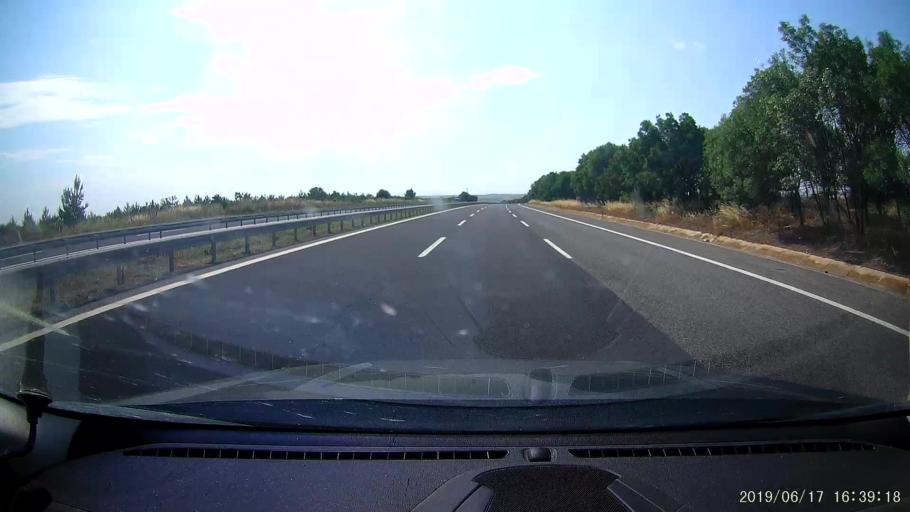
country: TR
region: Kirklareli
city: Luleburgaz
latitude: 41.4479
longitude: 27.4154
